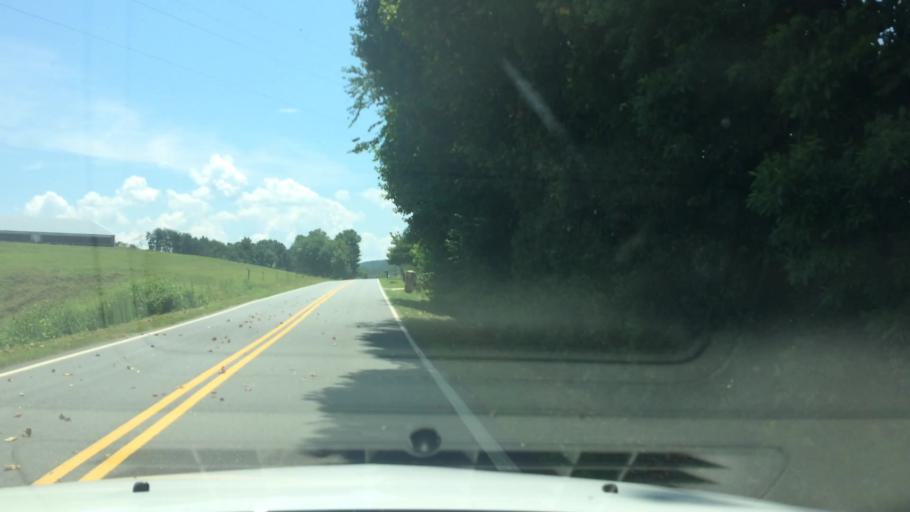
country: US
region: North Carolina
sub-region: Alexander County
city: Taylorsville
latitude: 35.9276
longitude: -81.2624
